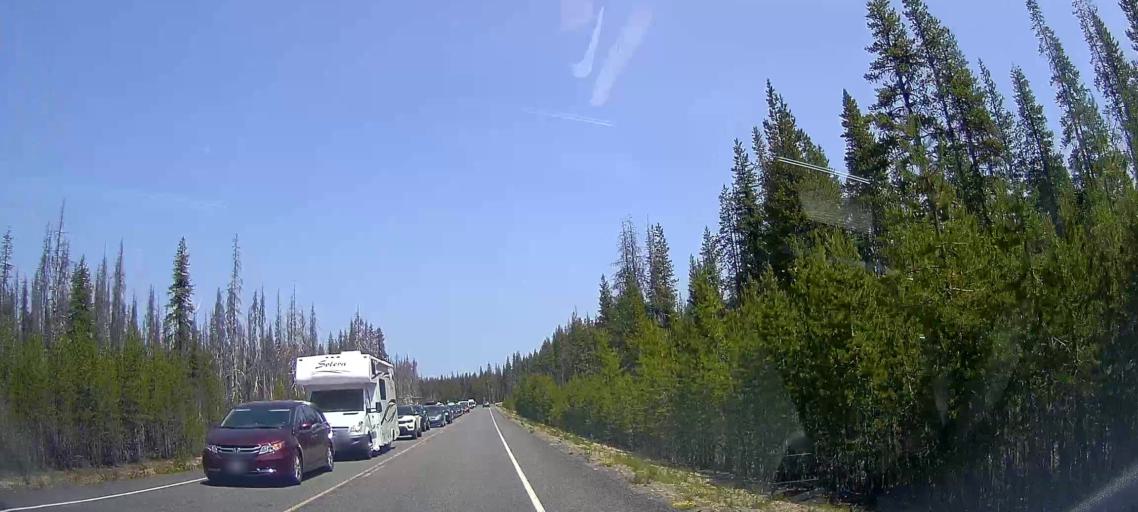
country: US
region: Oregon
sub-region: Lane County
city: Oakridge
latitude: 43.0846
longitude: -122.1167
